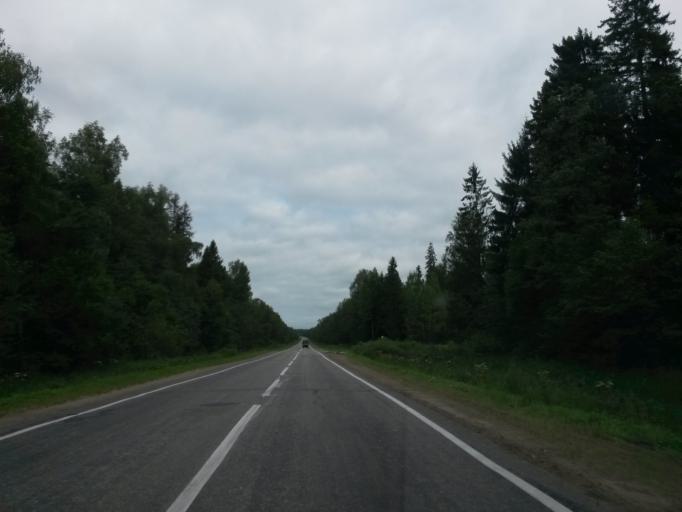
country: RU
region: Jaroslavl
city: Gavrilov-Yam
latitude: 57.4298
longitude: 39.9185
